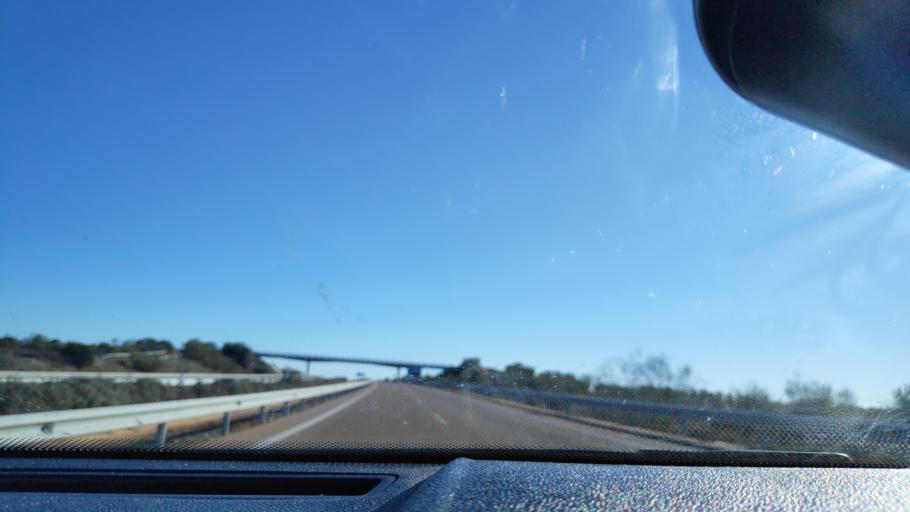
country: ES
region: Extremadura
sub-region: Provincia de Badajoz
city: Los Santos de Maimona
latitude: 38.4297
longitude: -6.3485
